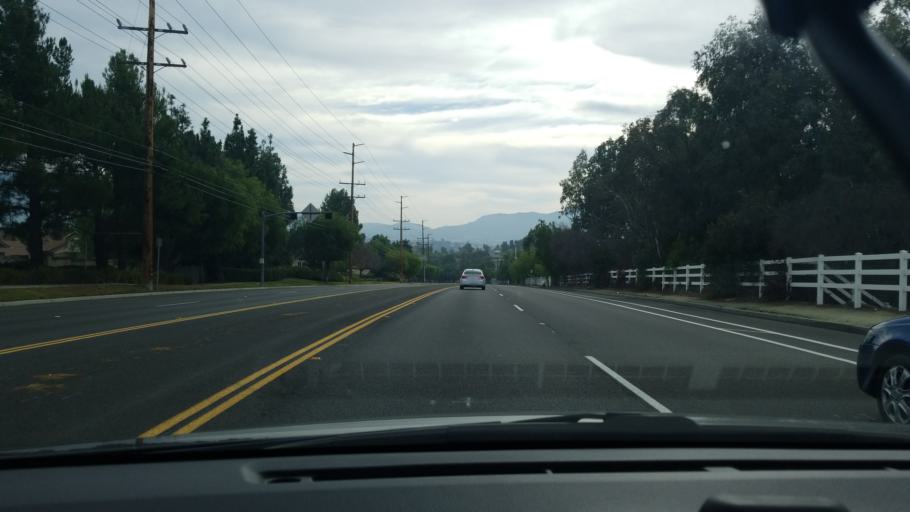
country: US
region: California
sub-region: Riverside County
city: Temecula
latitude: 33.4929
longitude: -117.1113
